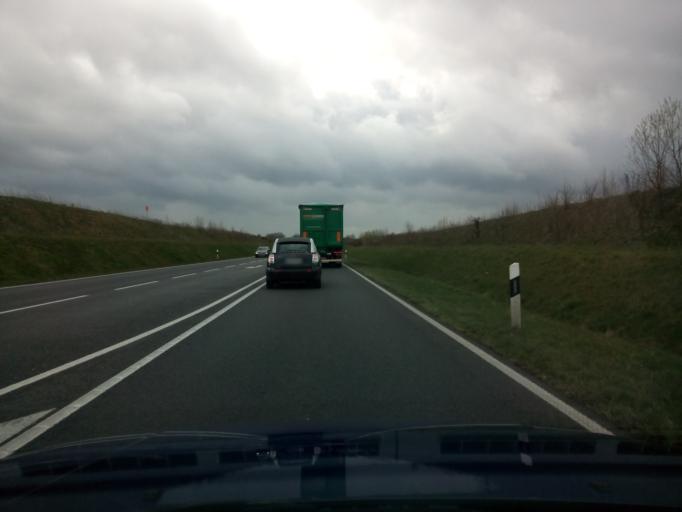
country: DE
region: Lower Saxony
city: Lastrup
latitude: 52.7933
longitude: 7.8405
